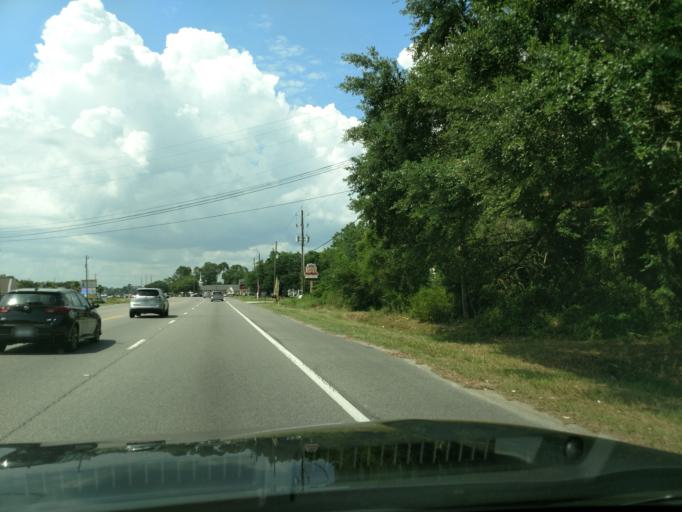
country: US
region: Mississippi
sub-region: Jackson County
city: Gulf Hills
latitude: 30.4276
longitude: -88.8292
